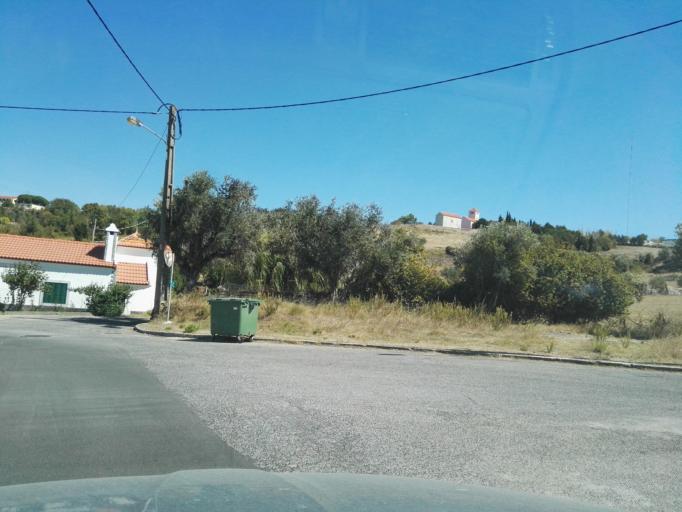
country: PT
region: Lisbon
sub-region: Vila Franca de Xira
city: Sao Joao dos Montes
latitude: 38.9629
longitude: -9.0226
